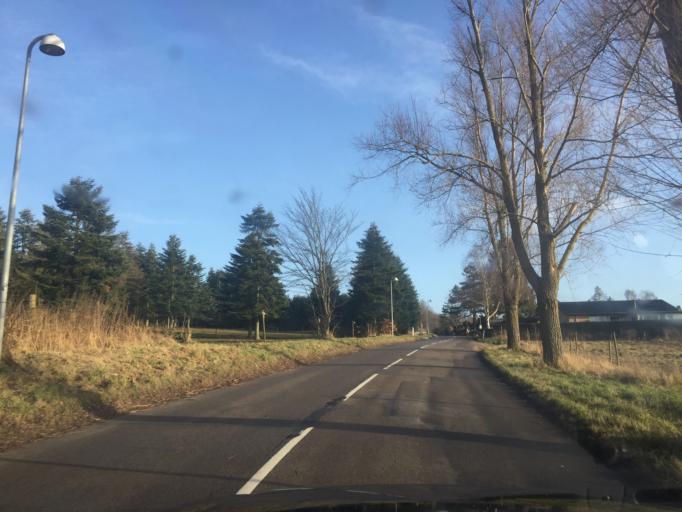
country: DK
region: Capital Region
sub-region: Hoje-Taastrup Kommune
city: Taastrup
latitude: 55.6848
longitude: 12.2975
